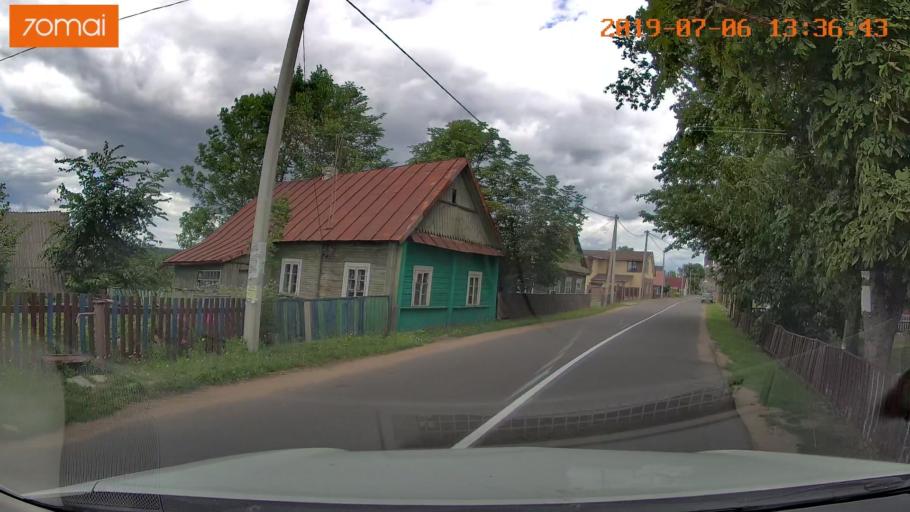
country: BY
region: Minsk
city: Enyerhyetykaw
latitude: 53.6905
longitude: 26.8645
